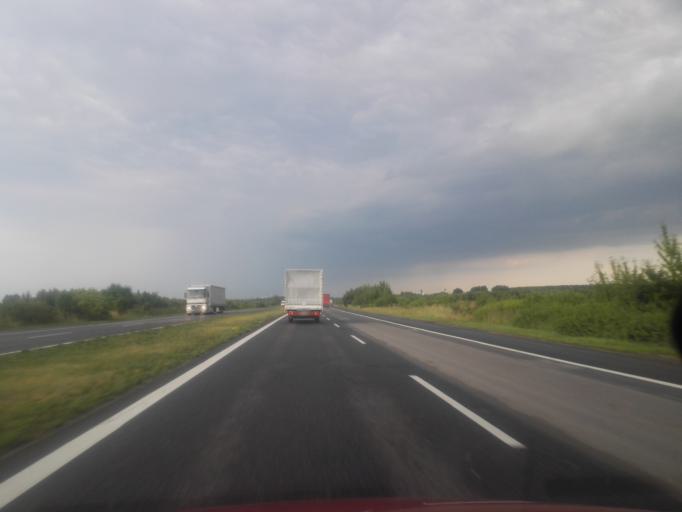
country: PL
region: Silesian Voivodeship
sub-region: Powiat czestochowski
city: Koscielec
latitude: 50.8778
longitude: 19.1627
